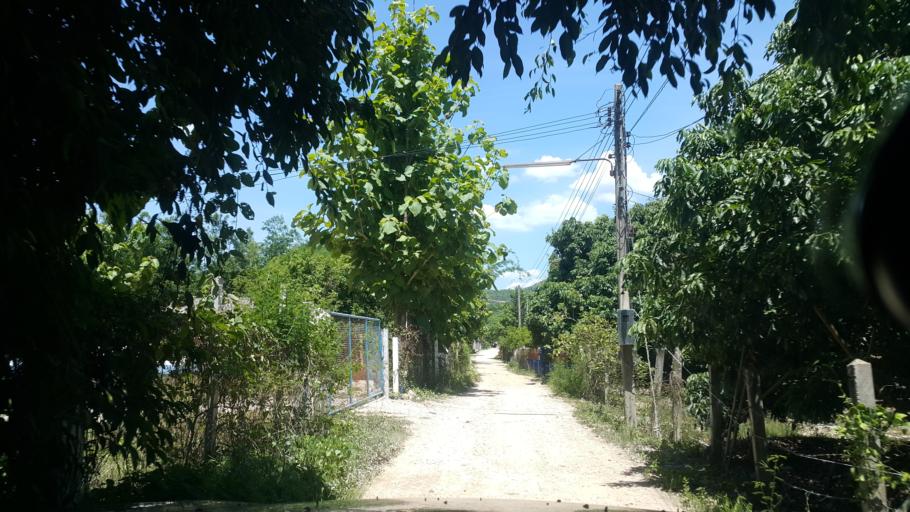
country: TH
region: Chiang Mai
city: San Kamphaeng
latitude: 18.7006
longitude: 99.1576
